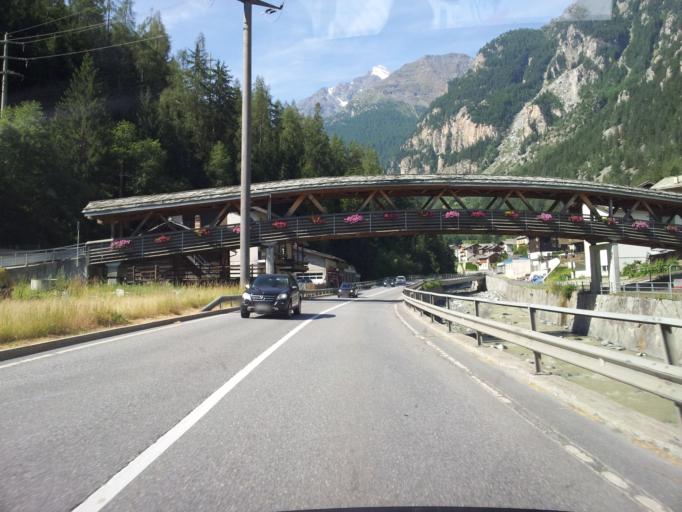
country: CH
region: Valais
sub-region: Visp District
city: Sankt Niklaus
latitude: 46.1766
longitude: 7.8051
